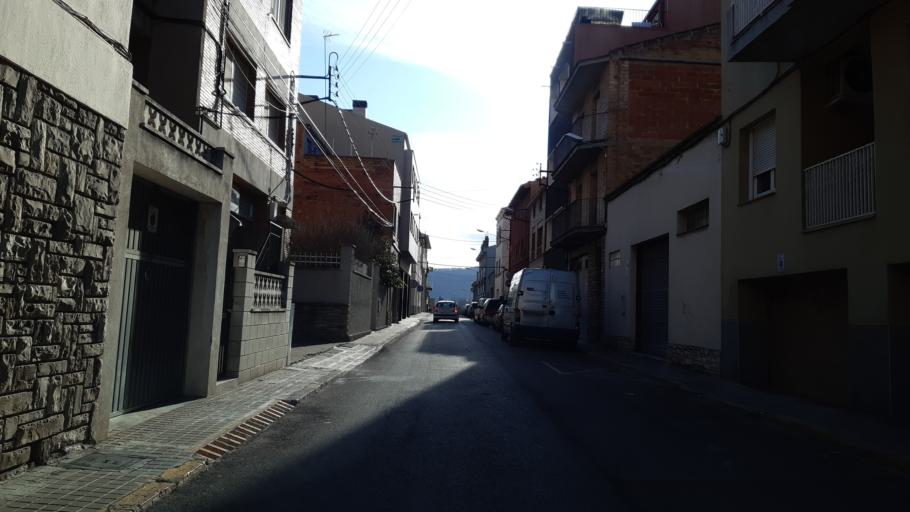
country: ES
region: Catalonia
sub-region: Provincia de Barcelona
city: Vilanova del Cami
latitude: 41.5757
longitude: 1.6308
